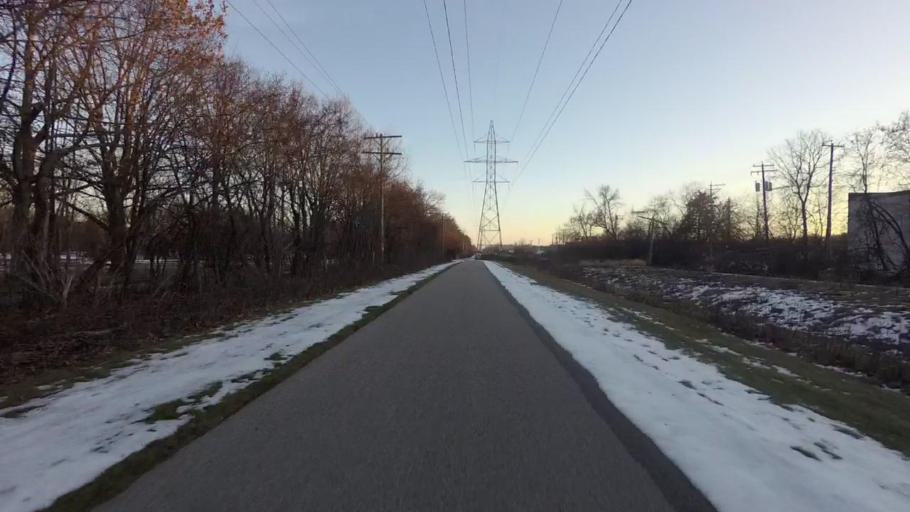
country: US
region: Wisconsin
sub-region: Milwaukee County
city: Brown Deer
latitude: 43.1531
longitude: -87.9565
